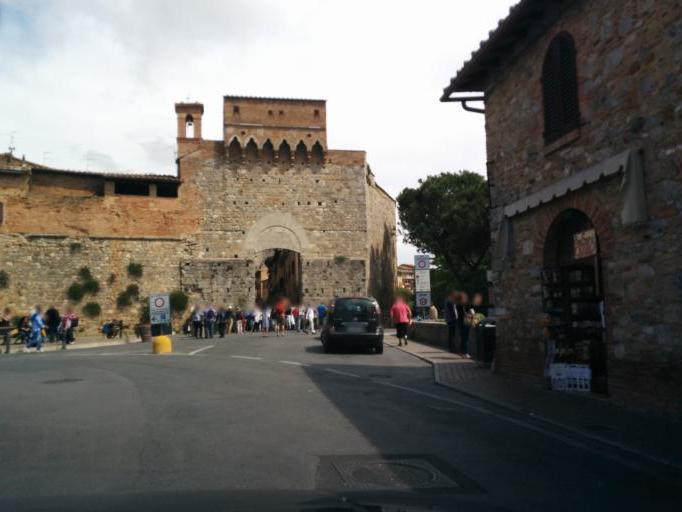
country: IT
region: Tuscany
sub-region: Provincia di Siena
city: San Gimignano
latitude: 43.4643
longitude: 11.0426
